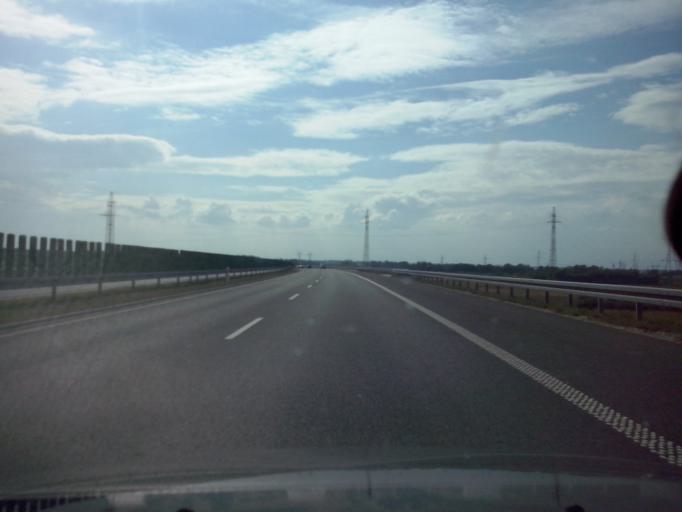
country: PL
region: Lesser Poland Voivodeship
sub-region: Powiat tarnowski
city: Lukowa
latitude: 50.0632
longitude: 20.9586
